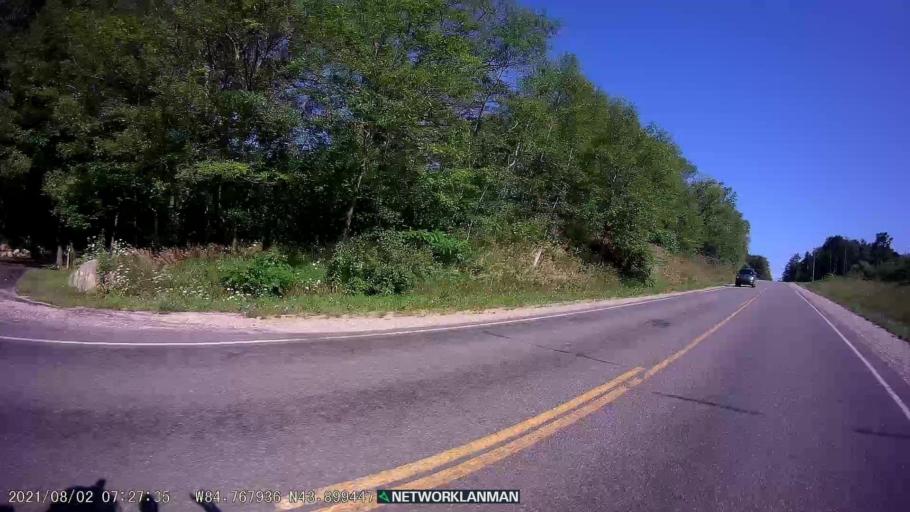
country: US
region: Michigan
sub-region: Clare County
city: Clare
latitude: 43.8989
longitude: -84.7680
